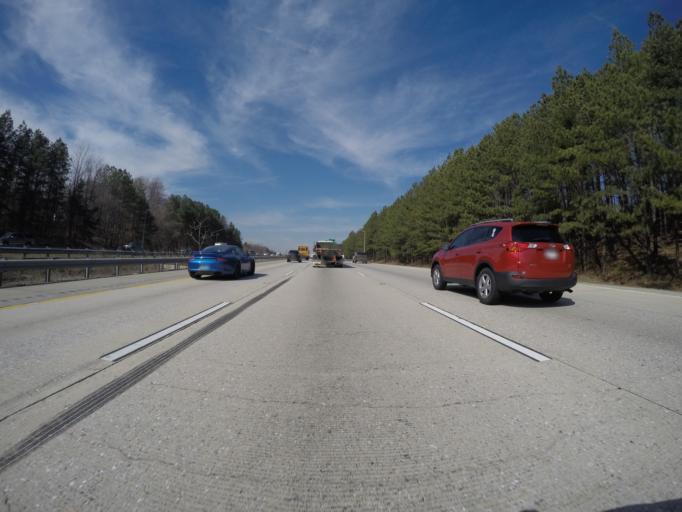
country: US
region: Maryland
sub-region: Anne Arundel County
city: South Gate
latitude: 39.0868
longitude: -76.6246
